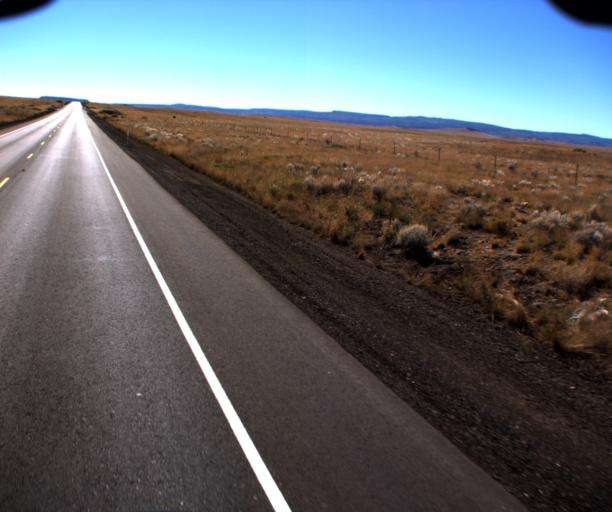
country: US
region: Arizona
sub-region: Apache County
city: Springerville
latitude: 34.2136
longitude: -109.3320
